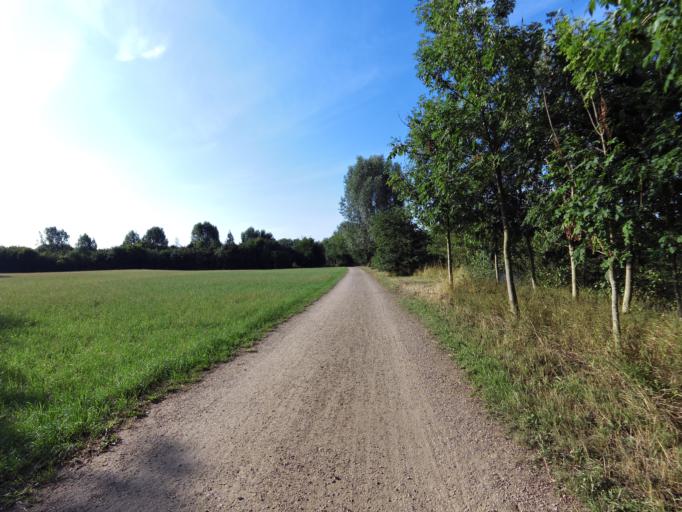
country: DE
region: North Rhine-Westphalia
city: Huckelhoven
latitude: 51.0507
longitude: 6.1926
